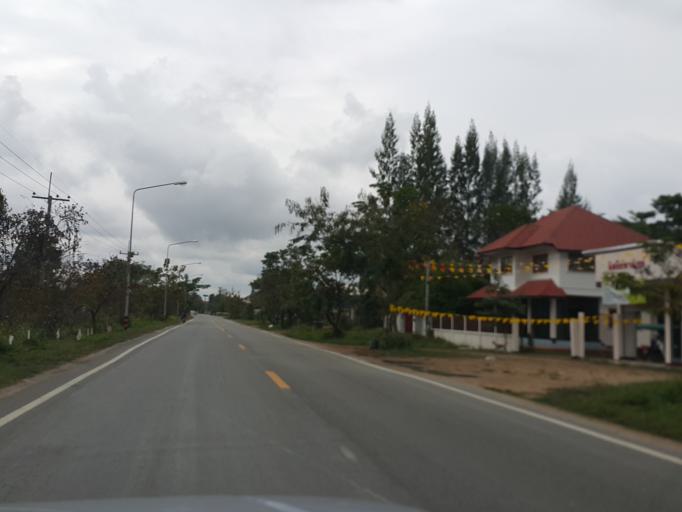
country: TH
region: Lamphun
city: Ban Thi
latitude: 18.5987
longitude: 99.0840
